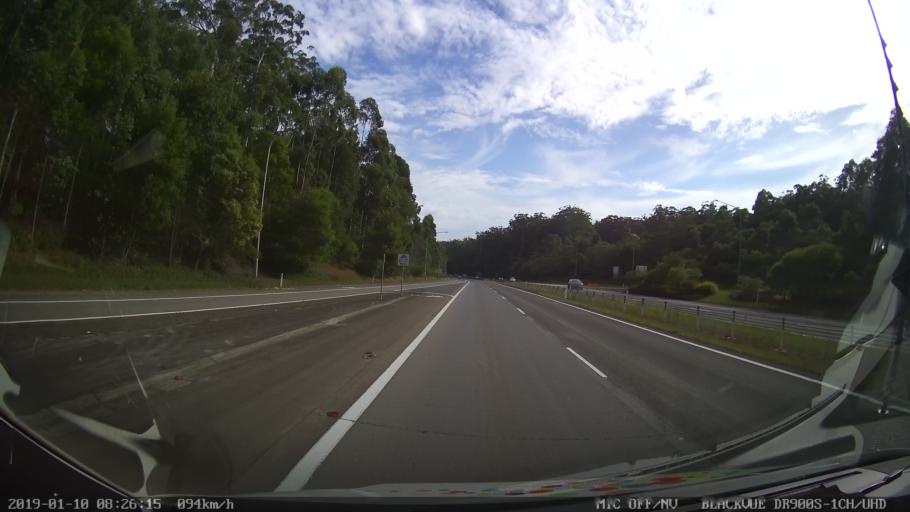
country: AU
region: New South Wales
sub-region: Coffs Harbour
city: Bonville
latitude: -30.4233
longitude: 153.0225
